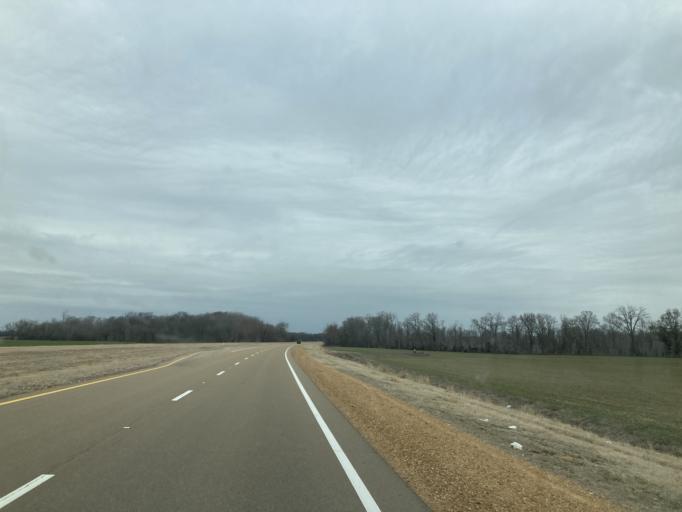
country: US
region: Mississippi
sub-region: Yazoo County
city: Yazoo City
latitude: 32.9849
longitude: -90.4640
